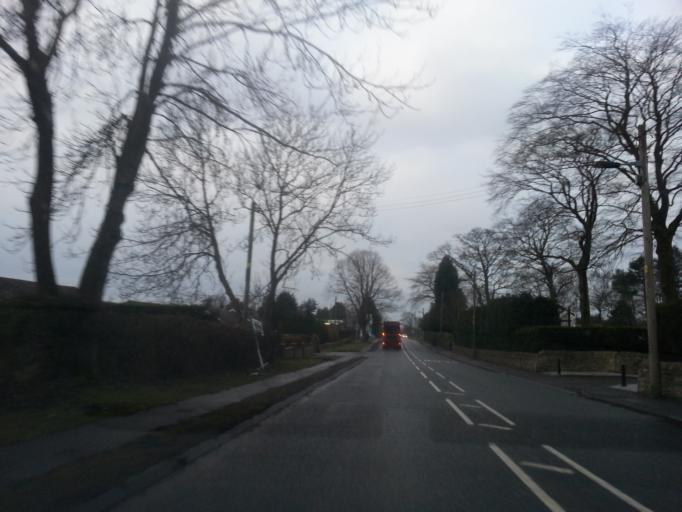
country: GB
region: England
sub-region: County Durham
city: Hamsterley
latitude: 54.7038
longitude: -1.7829
